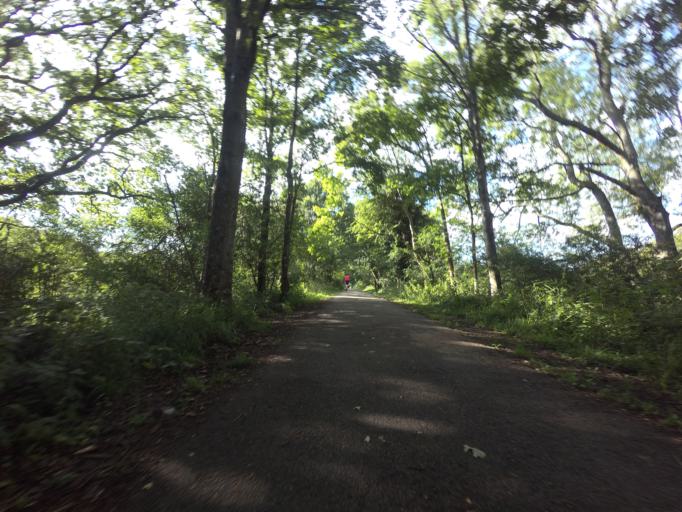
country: GB
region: England
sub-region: East Sussex
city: Horam
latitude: 50.9259
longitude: 0.2526
